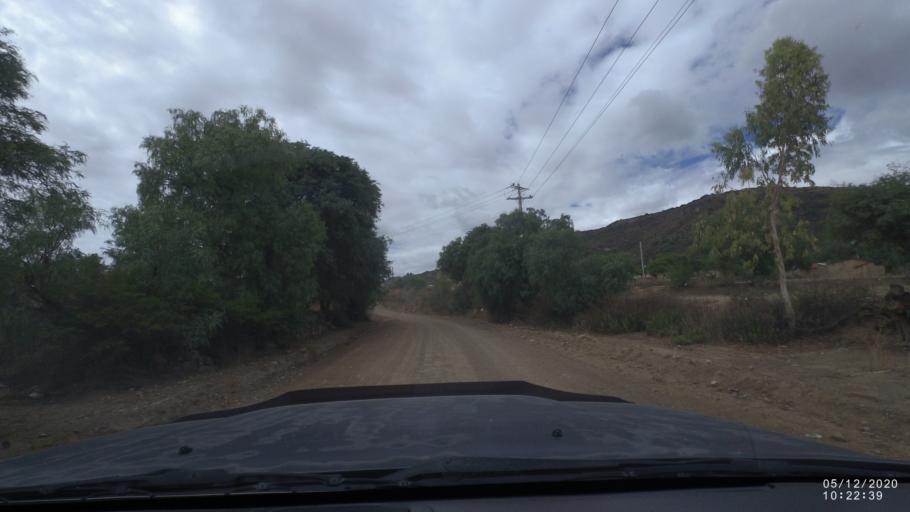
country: BO
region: Cochabamba
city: Sipe Sipe
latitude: -17.4973
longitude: -66.2832
